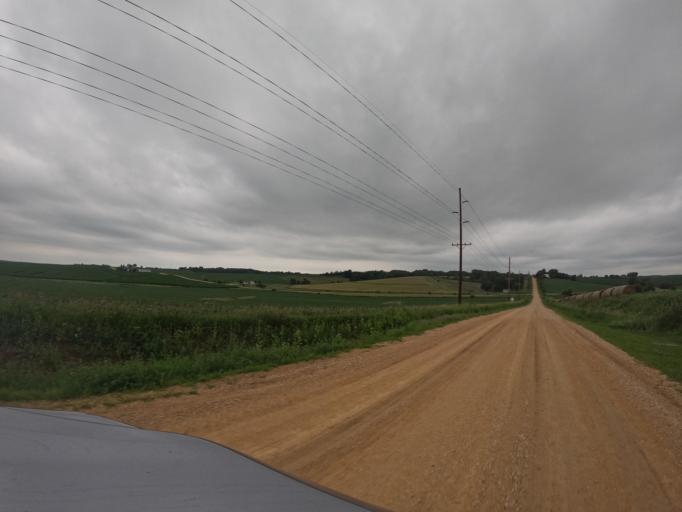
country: US
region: Iowa
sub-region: Jackson County
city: Maquoketa
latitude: 41.9381
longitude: -90.6230
